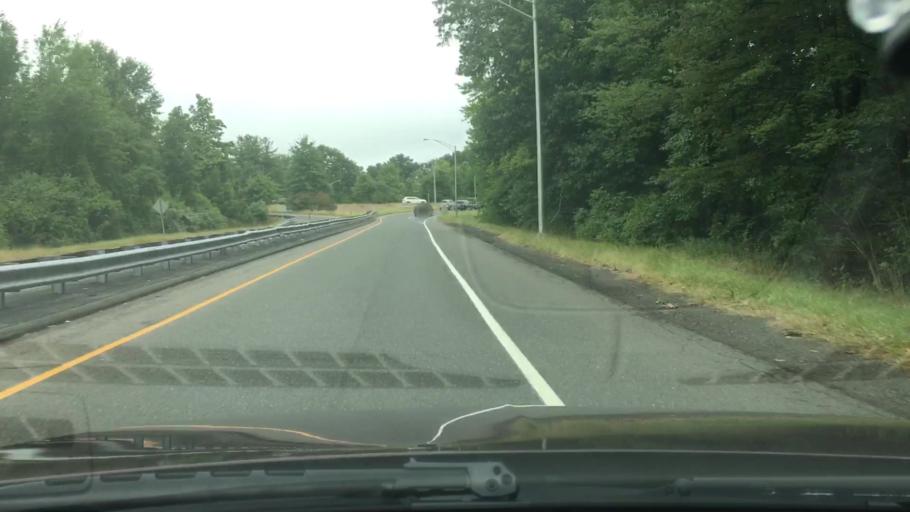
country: US
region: Connecticut
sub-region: Hartford County
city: Enfield
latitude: 41.9886
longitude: -72.5864
